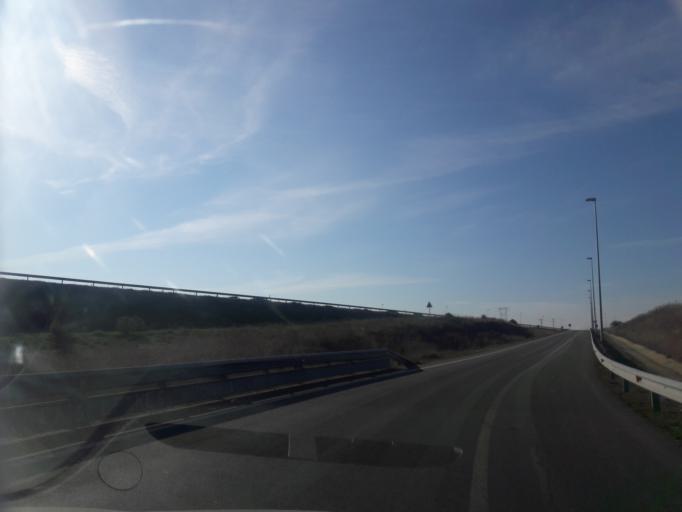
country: ES
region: Castille and Leon
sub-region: Provincia de Salamanca
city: Montejo
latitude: 40.6312
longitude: -5.6329
